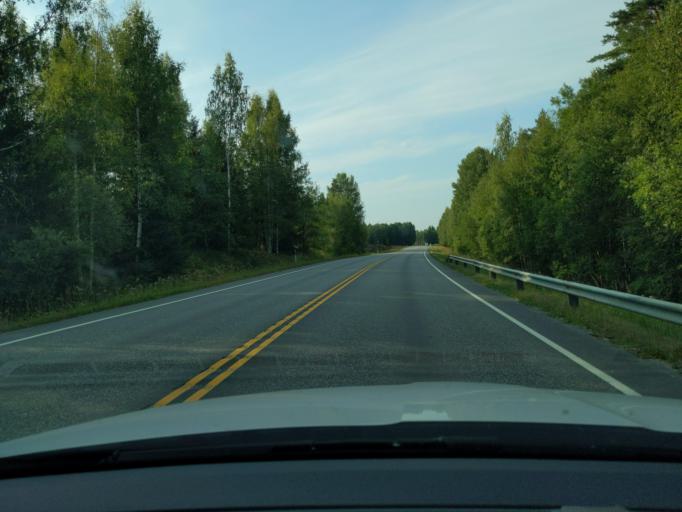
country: FI
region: Paijanne Tavastia
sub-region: Lahti
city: Padasjoki
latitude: 61.3086
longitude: 25.2929
